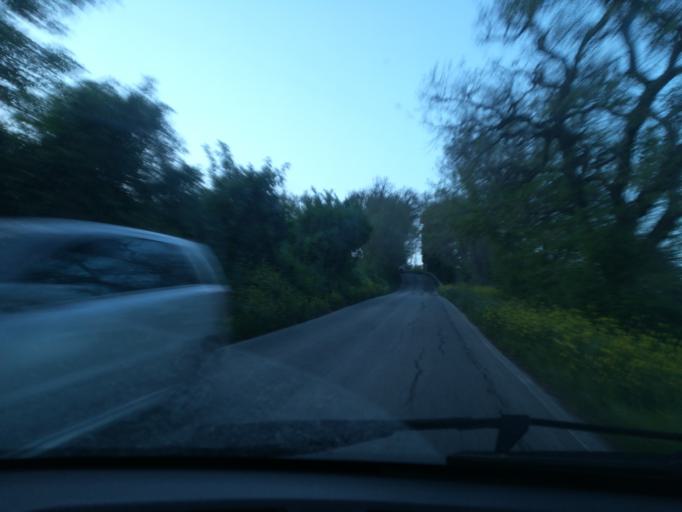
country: IT
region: The Marches
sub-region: Provincia di Macerata
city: Macerata
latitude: 43.2793
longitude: 13.4487
